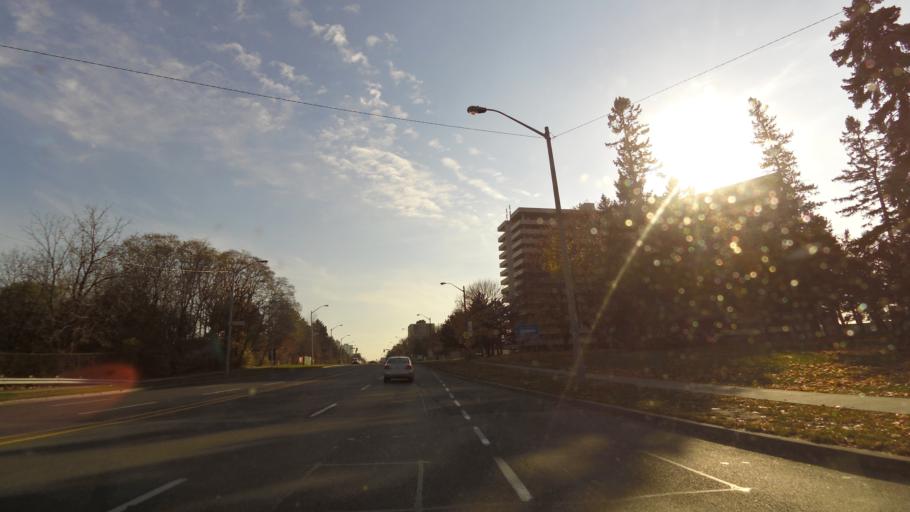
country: CA
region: Ontario
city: Concord
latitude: 43.7751
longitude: -79.5219
